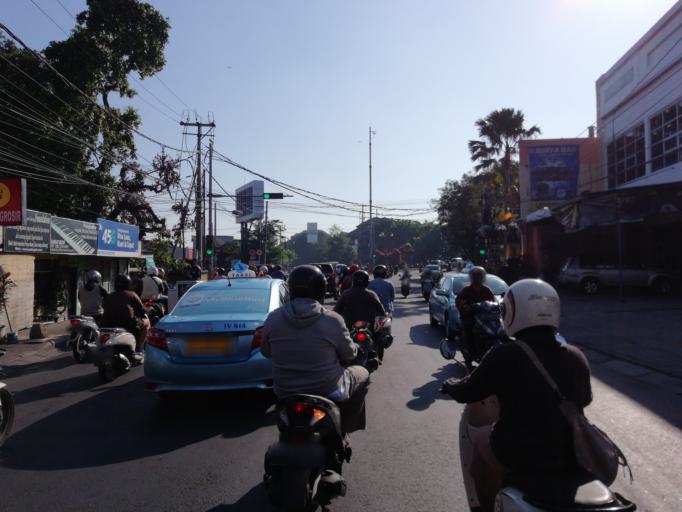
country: ID
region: Bali
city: Karyadharma
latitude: -8.6821
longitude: 115.1968
